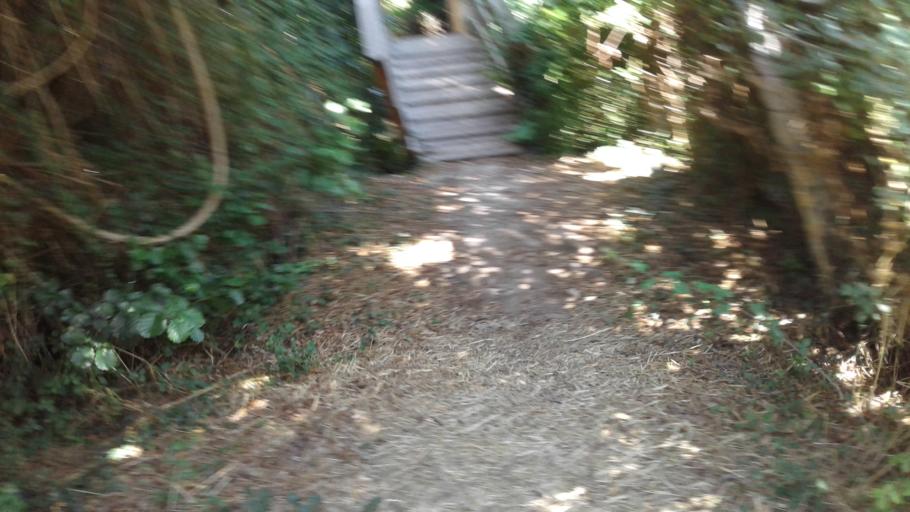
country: IT
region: Sardinia
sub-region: Provincia di Olbia-Tempio
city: Calangianus
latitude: 40.9082
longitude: 9.1726
